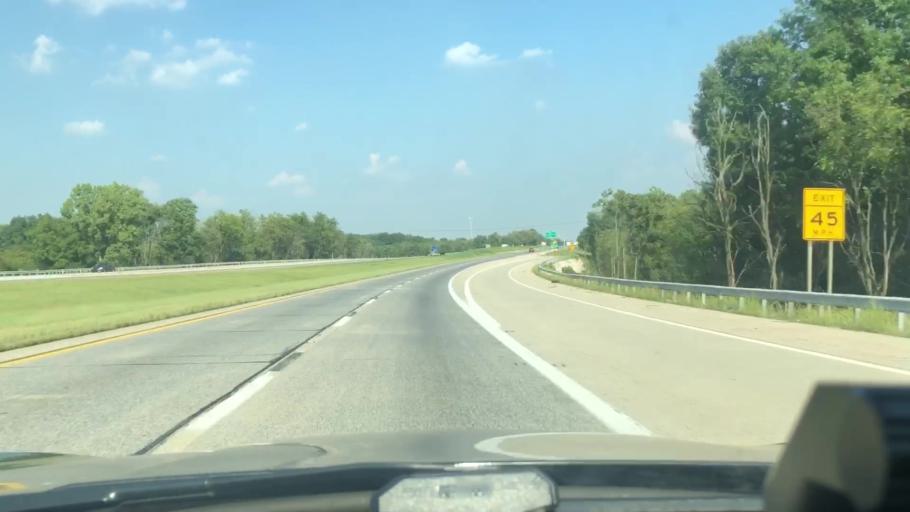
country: US
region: Pennsylvania
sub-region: Lebanon County
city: Palmyra
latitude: 40.4132
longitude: -76.5861
